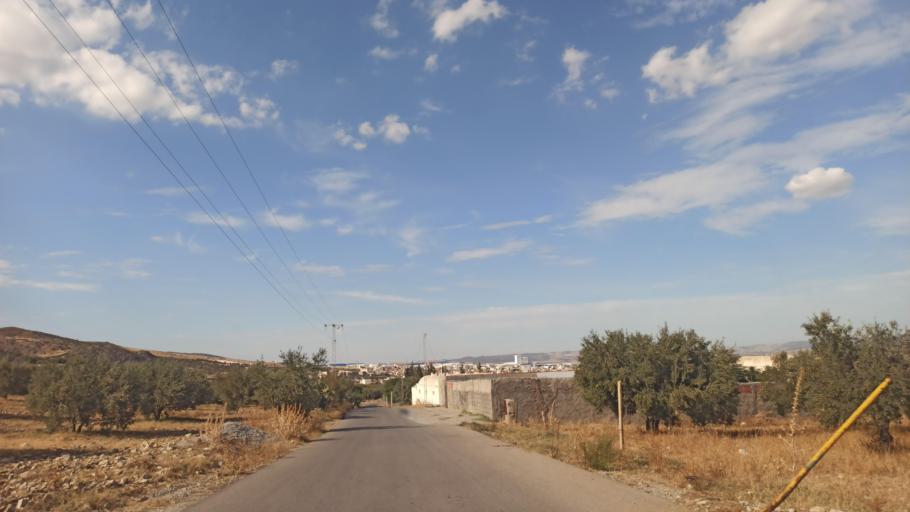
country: TN
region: Zaghwan
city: Zaghouan
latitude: 36.3371
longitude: 10.2106
